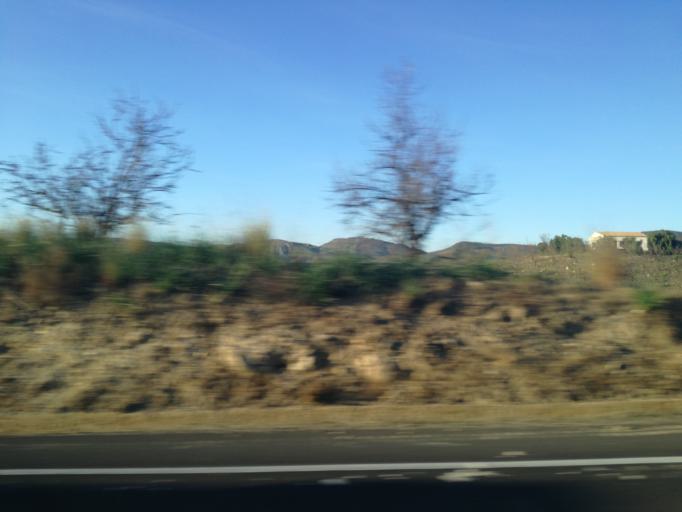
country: IT
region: Sicily
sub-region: Provincia di Caltanissetta
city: Niscemi
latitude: 37.2116
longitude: 14.4000
